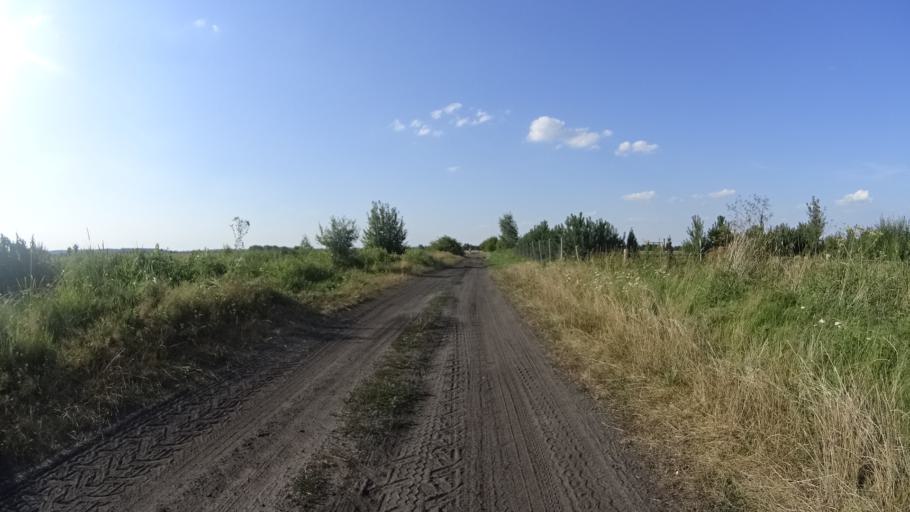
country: PL
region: Masovian Voivodeship
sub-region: Powiat bialobrzeski
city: Wysmierzyce
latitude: 51.6307
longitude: 20.8164
